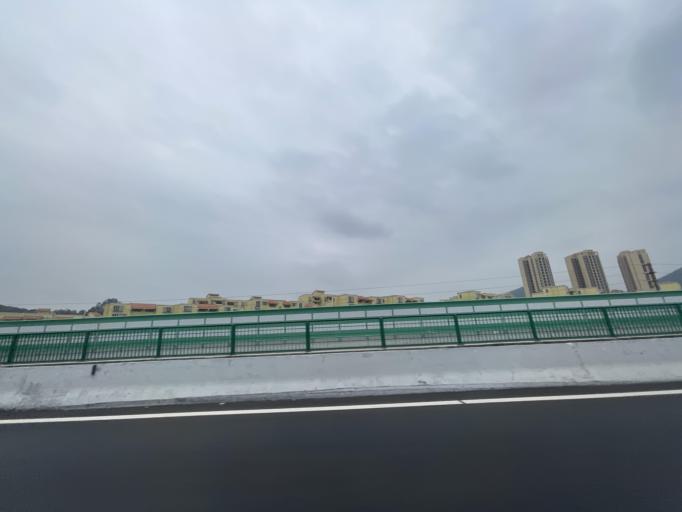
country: CN
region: Guangdong
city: Nansha
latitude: 22.7821
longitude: 113.5358
